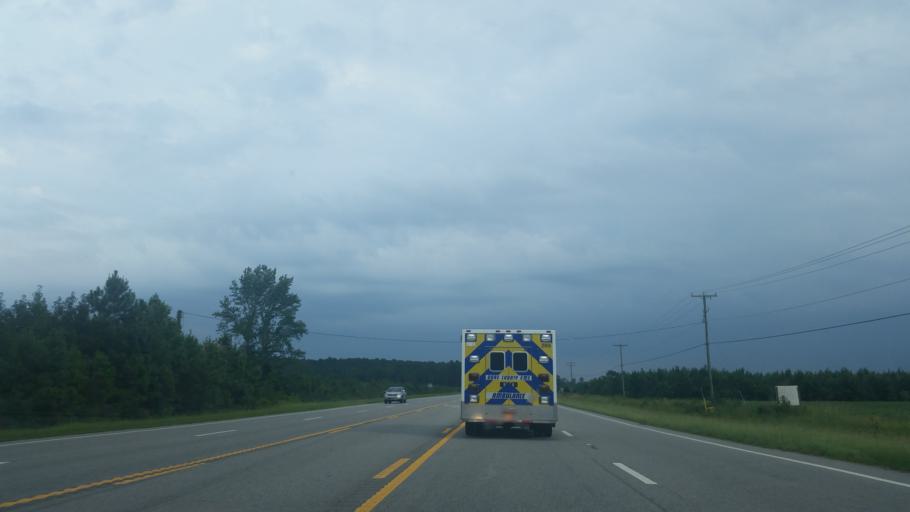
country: US
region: North Carolina
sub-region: Currituck County
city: Moyock
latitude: 36.4780
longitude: -76.1277
